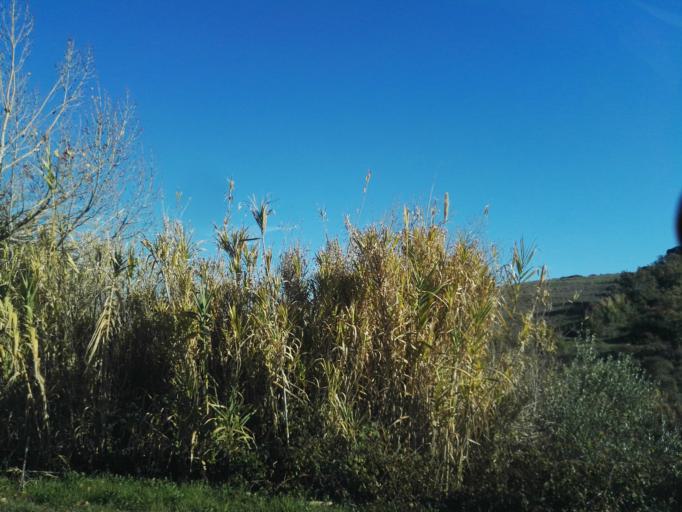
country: PT
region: Lisbon
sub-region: Arruda Dos Vinhos
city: Arruda dos Vinhos
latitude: 38.9776
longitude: -9.0894
